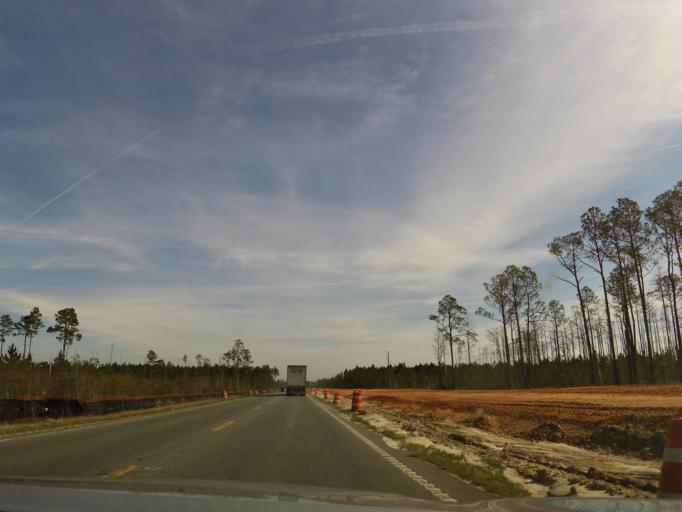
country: US
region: Georgia
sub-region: Ware County
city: Deenwood
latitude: 31.1485
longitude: -82.4669
